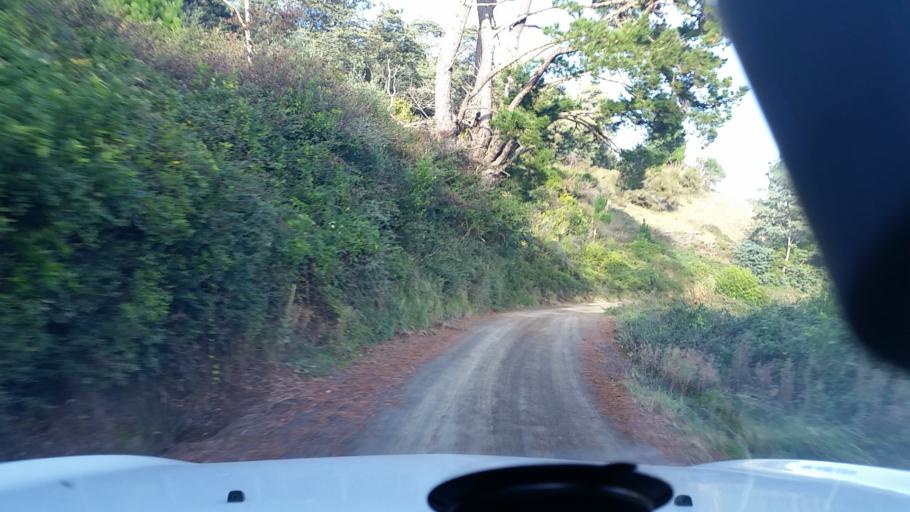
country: NZ
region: Hawke's Bay
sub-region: Napier City
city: Napier
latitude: -39.2422
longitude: 176.8139
